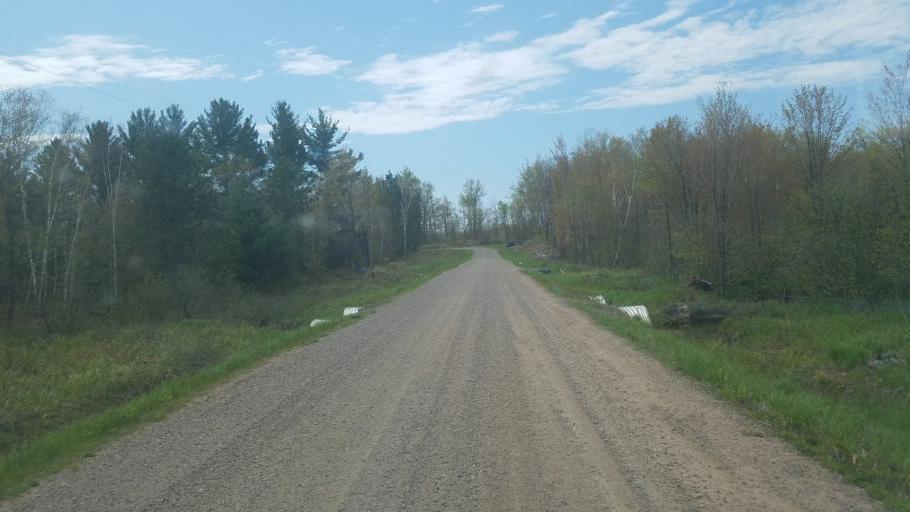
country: US
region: Wisconsin
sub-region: Clark County
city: Neillsville
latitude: 44.4534
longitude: -90.4665
